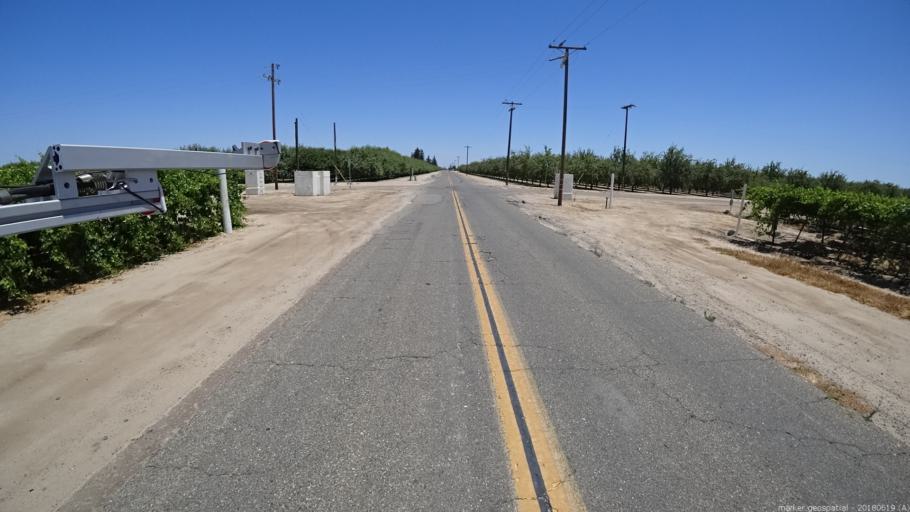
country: US
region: California
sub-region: Madera County
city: Parkwood
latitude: 36.8658
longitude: -120.0745
